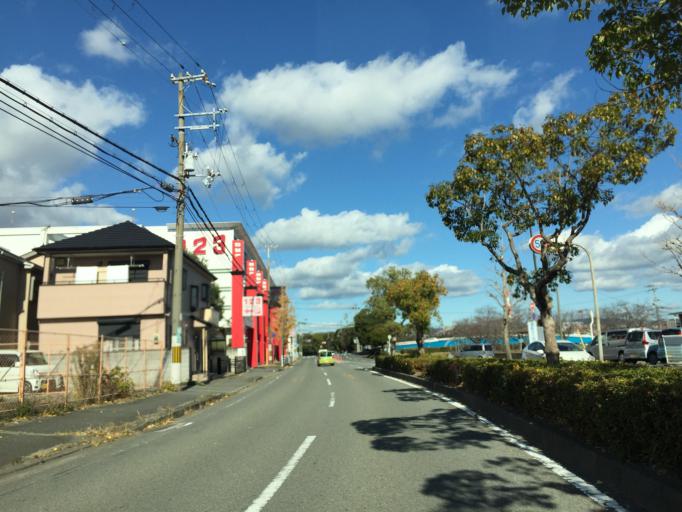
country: JP
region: Wakayama
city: Wakayama-shi
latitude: 34.2041
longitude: 135.1796
